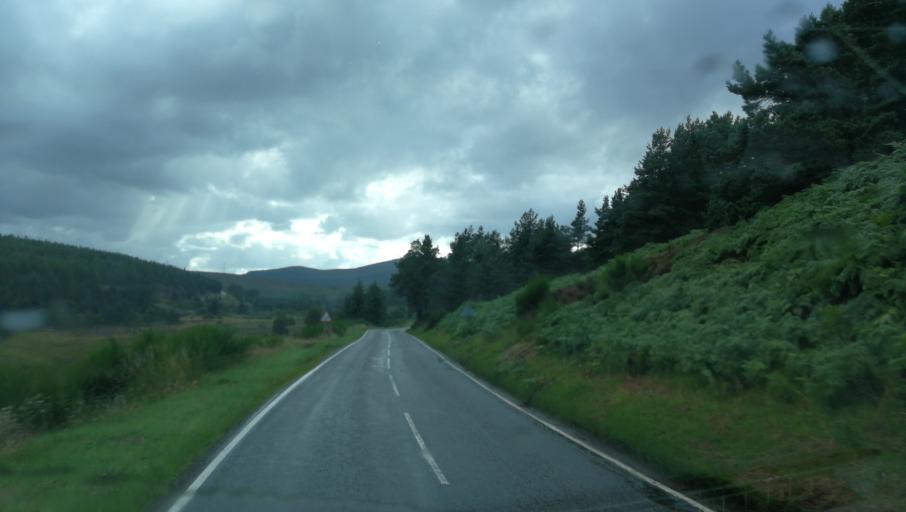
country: GB
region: Scotland
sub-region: Highland
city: Alness
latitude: 57.7695
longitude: -4.2446
